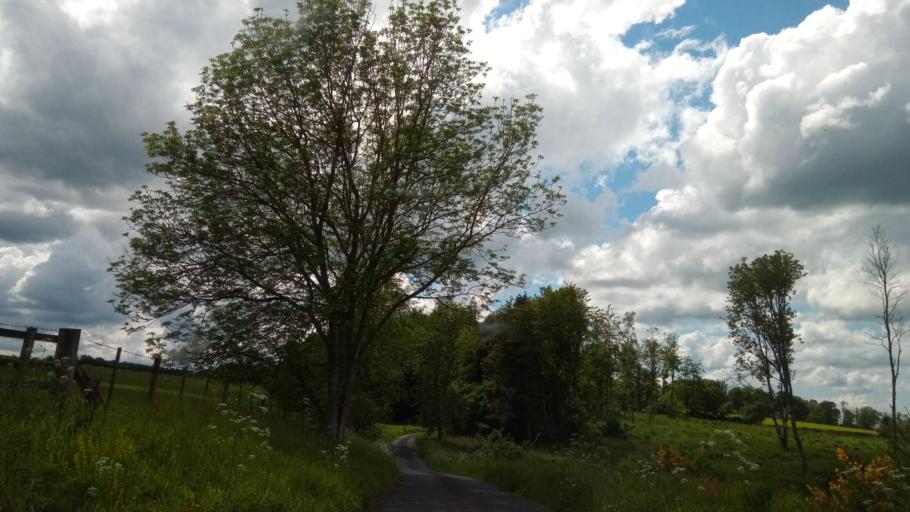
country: GB
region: Scotland
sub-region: The Scottish Borders
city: Coldstream
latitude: 55.5930
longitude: -2.2871
